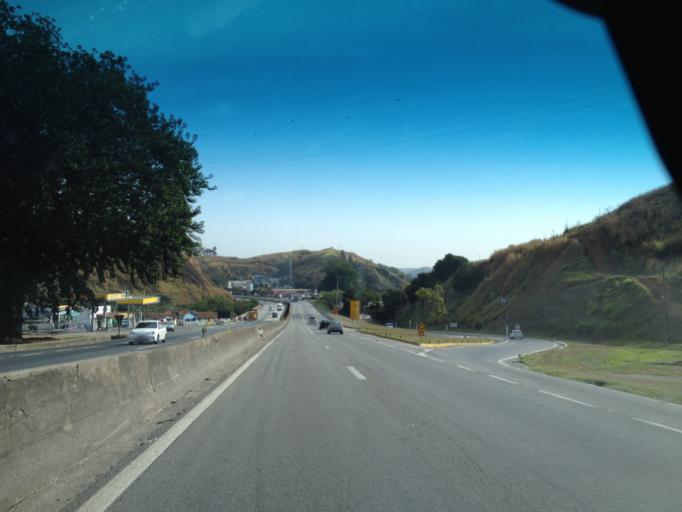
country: BR
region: Rio de Janeiro
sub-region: Barra Mansa
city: Barra Mansa
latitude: -22.5506
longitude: -44.1828
